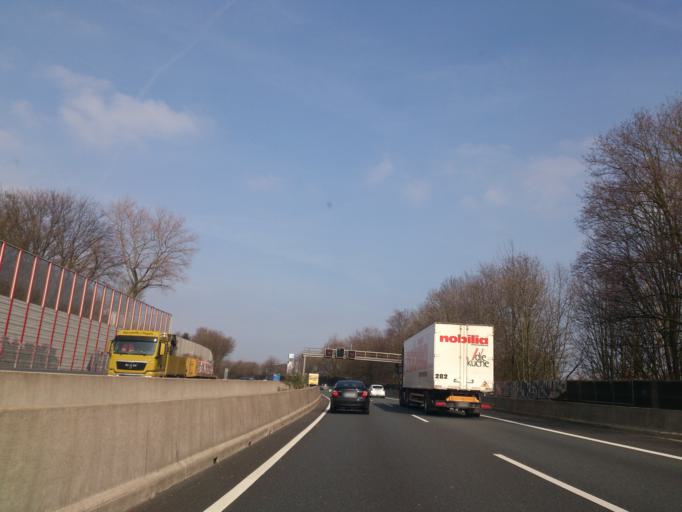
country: DE
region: North Rhine-Westphalia
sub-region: Regierungsbezirk Dusseldorf
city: Wuppertal
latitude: 51.2724
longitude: 7.1646
